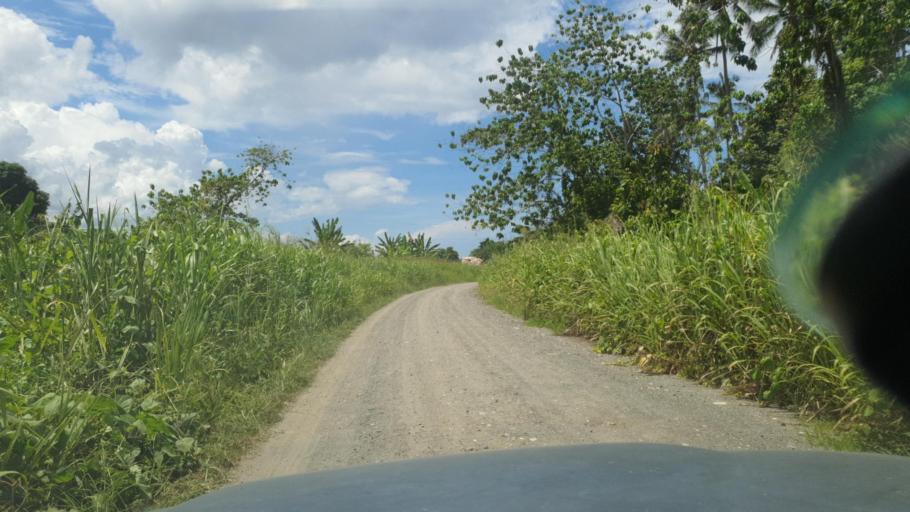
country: SB
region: Guadalcanal
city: Honiara
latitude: -9.4494
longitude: 160.1866
